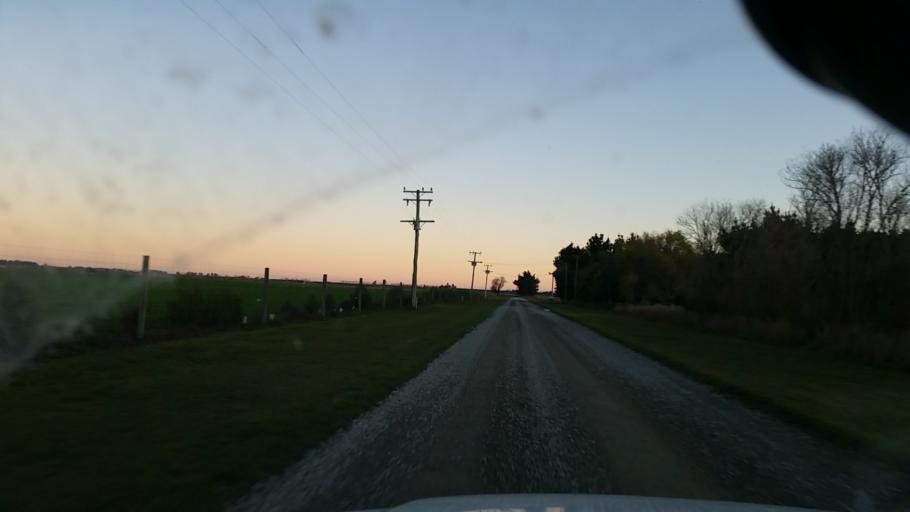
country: NZ
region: Canterbury
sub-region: Ashburton District
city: Tinwald
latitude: -44.0578
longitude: 171.6616
